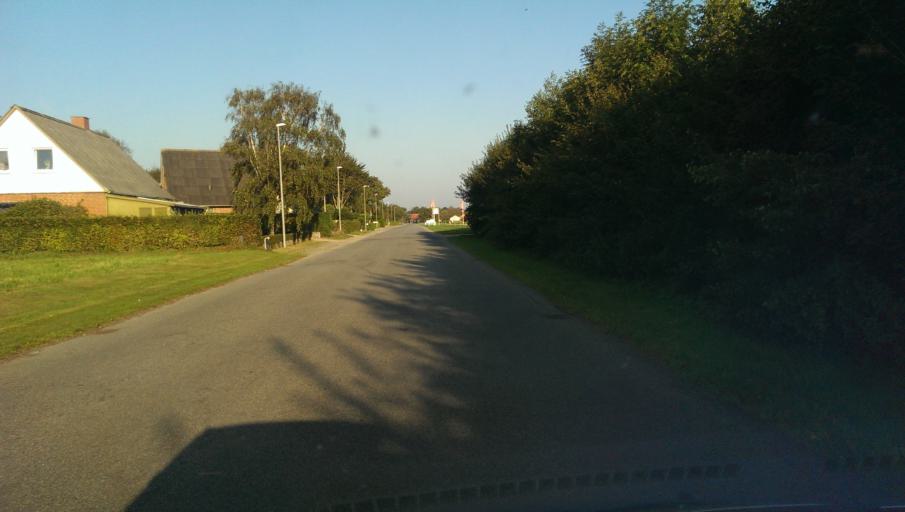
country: DK
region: South Denmark
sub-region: Esbjerg Kommune
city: Bramming
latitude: 55.4677
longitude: 8.7928
